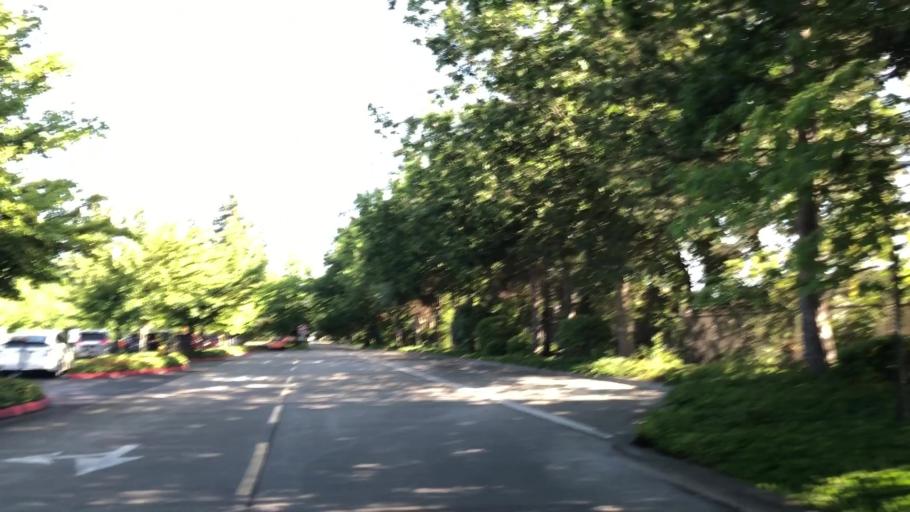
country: US
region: Washington
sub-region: King County
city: Redmond
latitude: 47.6732
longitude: -122.1003
